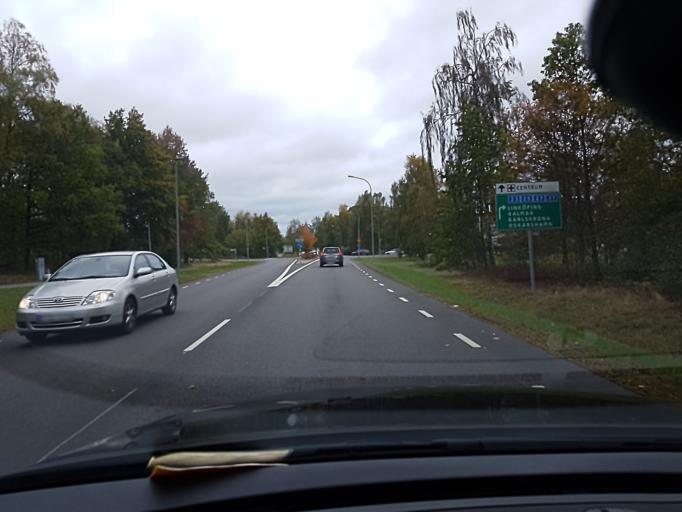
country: SE
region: Kronoberg
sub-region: Vaxjo Kommun
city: Vaexjoe
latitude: 56.9000
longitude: 14.7986
